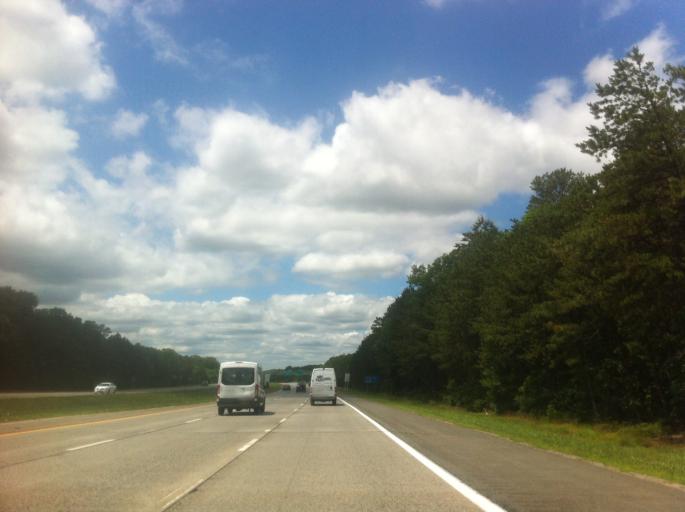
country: US
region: New York
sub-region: Suffolk County
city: Manorville
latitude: 40.8752
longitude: -72.7926
